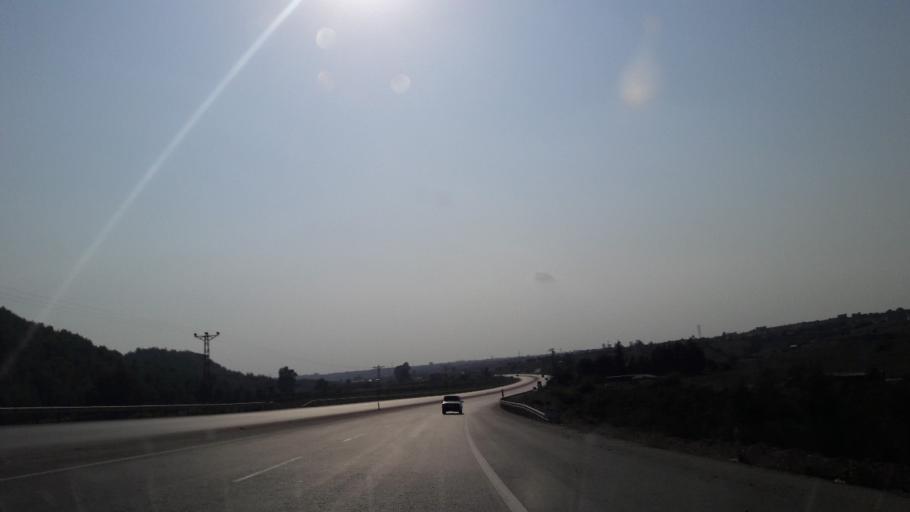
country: TR
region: Adana
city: Yuregir
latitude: 37.0746
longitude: 35.4677
